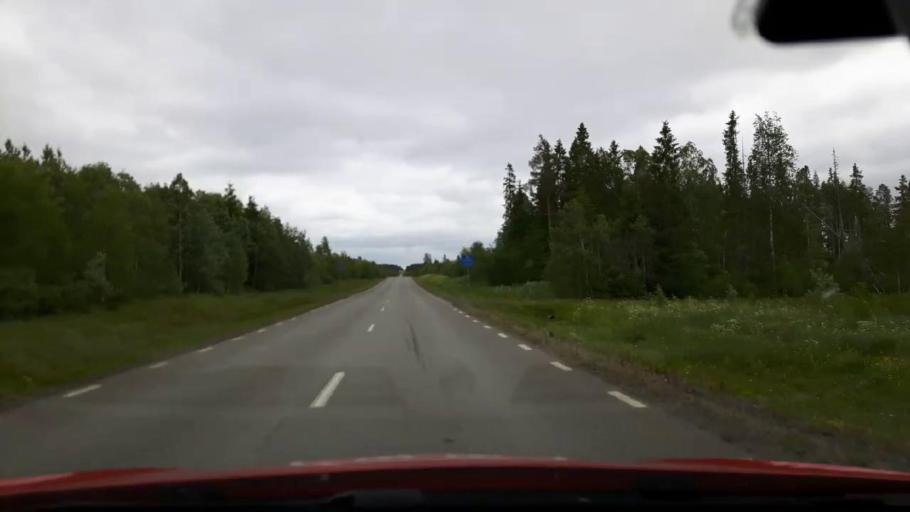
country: SE
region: Jaemtland
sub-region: OEstersunds Kommun
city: Lit
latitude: 63.7290
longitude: 14.9174
